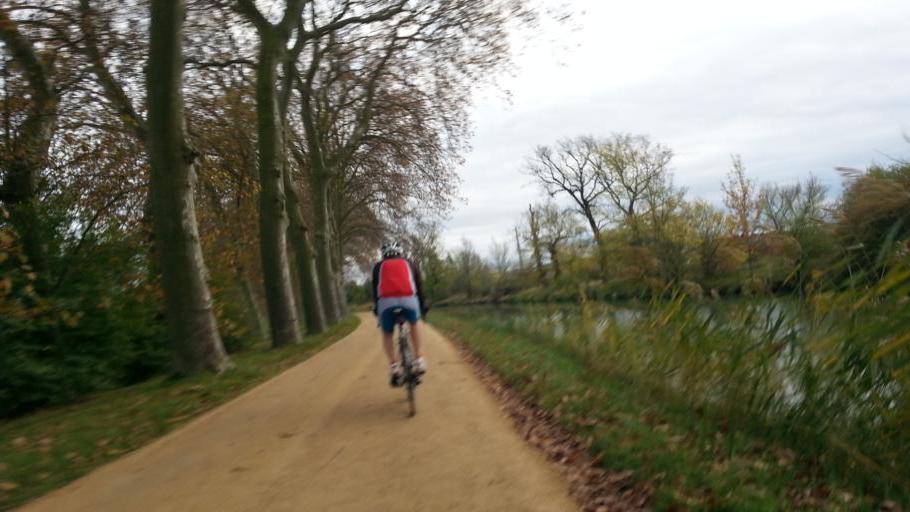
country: FR
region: Midi-Pyrenees
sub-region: Departement de la Haute-Garonne
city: Castanet-Tolosan
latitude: 43.5322
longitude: 1.5056
